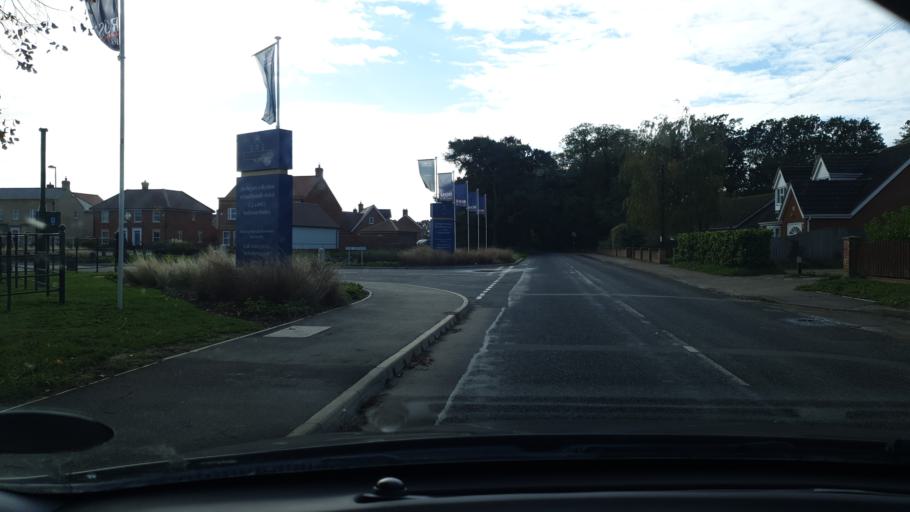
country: GB
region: England
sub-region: Essex
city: Manningtree
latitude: 51.9371
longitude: 1.0444
